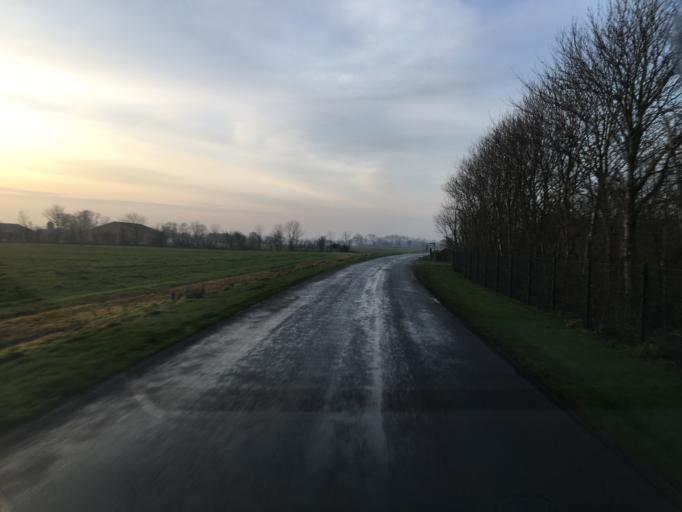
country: DK
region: South Denmark
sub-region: Tonder Kommune
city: Logumkloster
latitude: 55.1101
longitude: 8.9903
